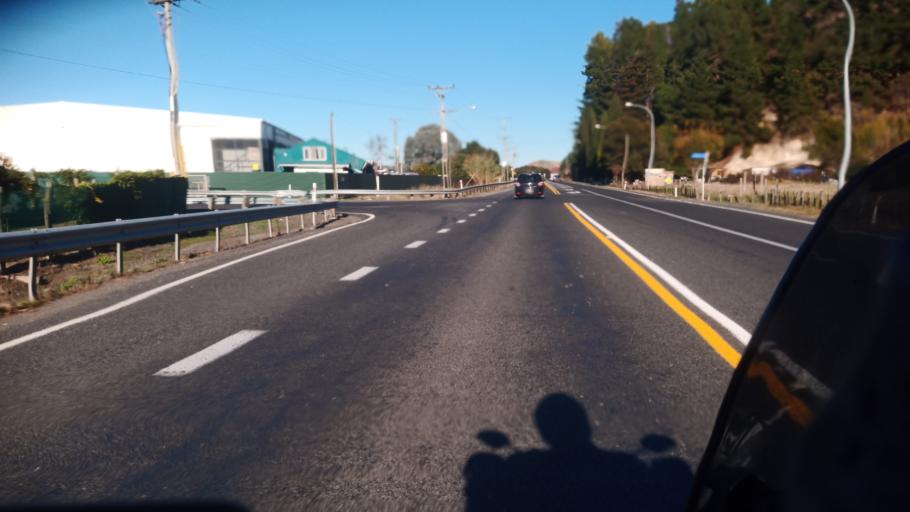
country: NZ
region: Hawke's Bay
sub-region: Napier City
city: Napier
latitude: -39.4159
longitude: 176.8695
